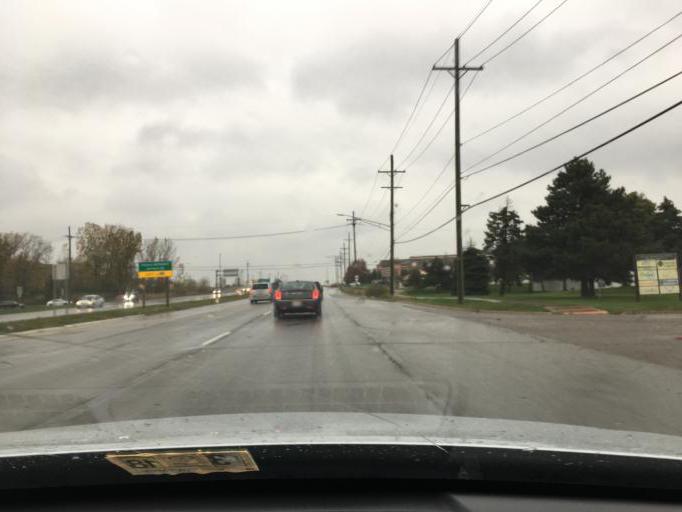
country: US
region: Michigan
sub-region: Oakland County
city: Auburn Hills
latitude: 42.6993
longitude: -83.2421
